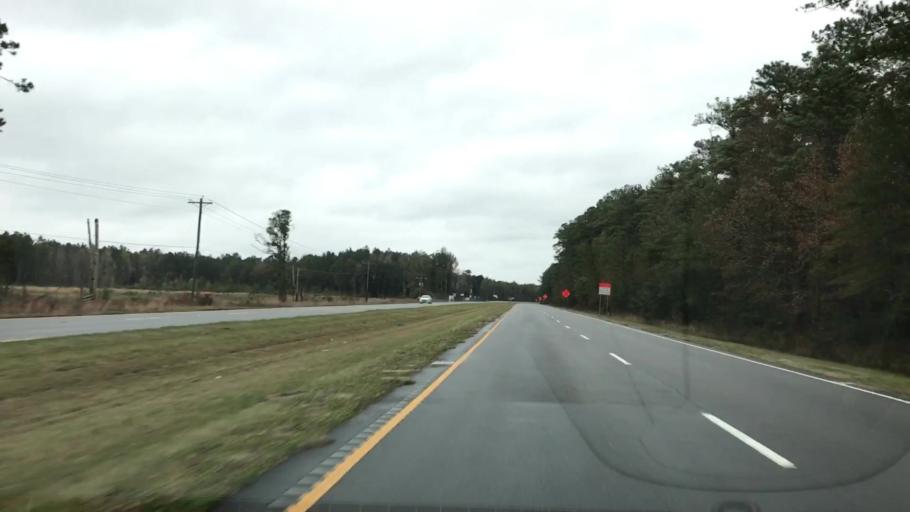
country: US
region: South Carolina
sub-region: Georgetown County
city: Georgetown
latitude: 33.2887
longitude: -79.3481
